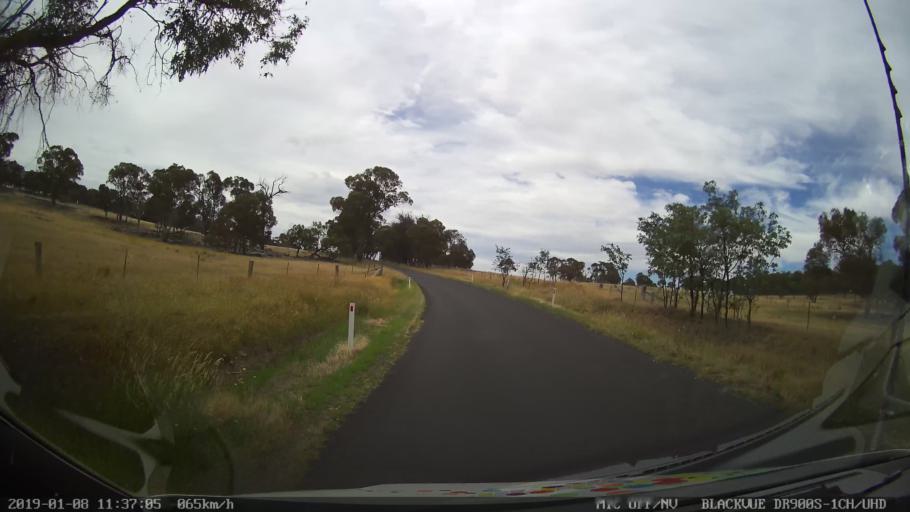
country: AU
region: New South Wales
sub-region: Guyra
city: Guyra
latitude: -30.3499
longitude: 151.5489
